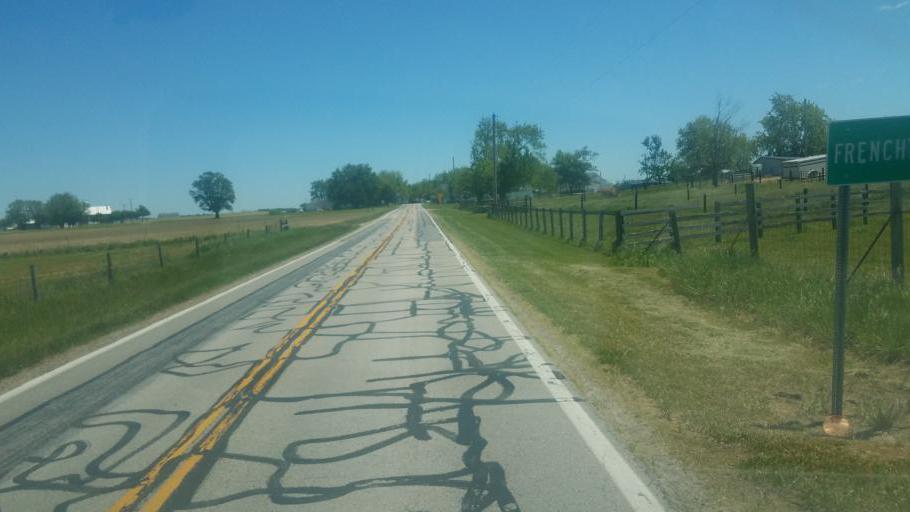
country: US
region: Ohio
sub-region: Darke County
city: Versailles
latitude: 40.2487
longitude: -84.5268
